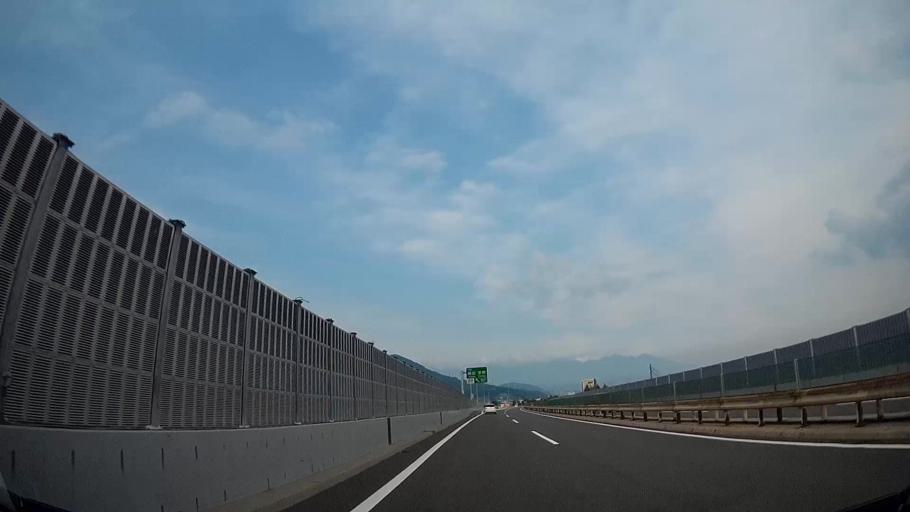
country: JP
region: Nagano
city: Chino
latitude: 36.0036
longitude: 138.1239
